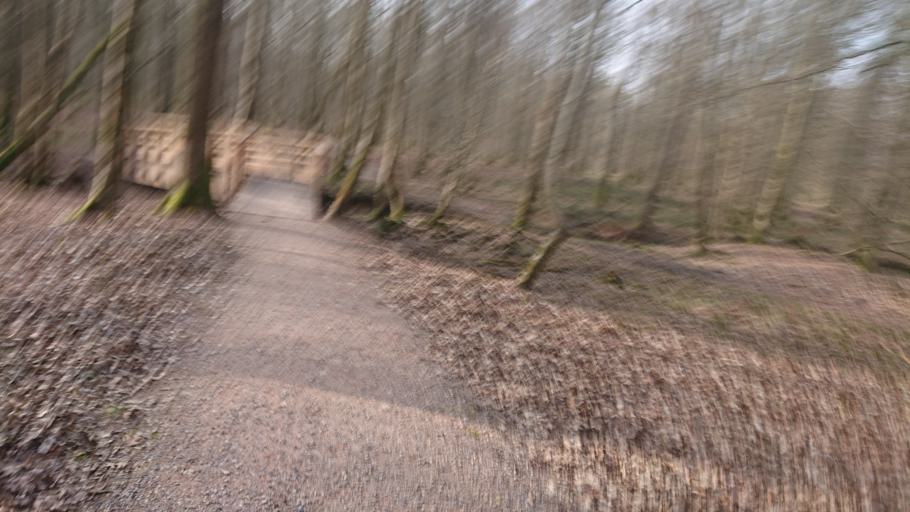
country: FR
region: Nord-Pas-de-Calais
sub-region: Departement du Nord
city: Maroilles
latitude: 50.1711
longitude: 3.7234
